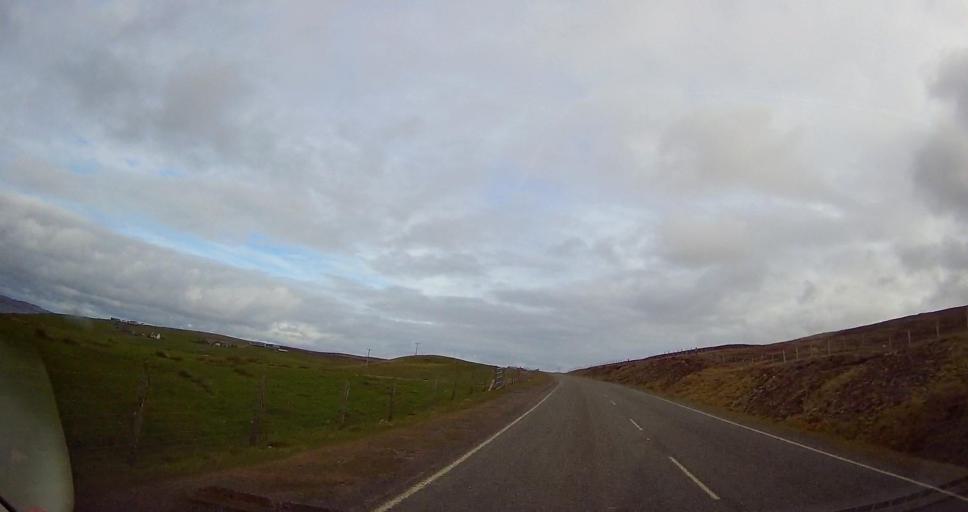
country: GB
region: Scotland
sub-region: Shetland Islands
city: Shetland
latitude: 60.5793
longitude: -1.1706
